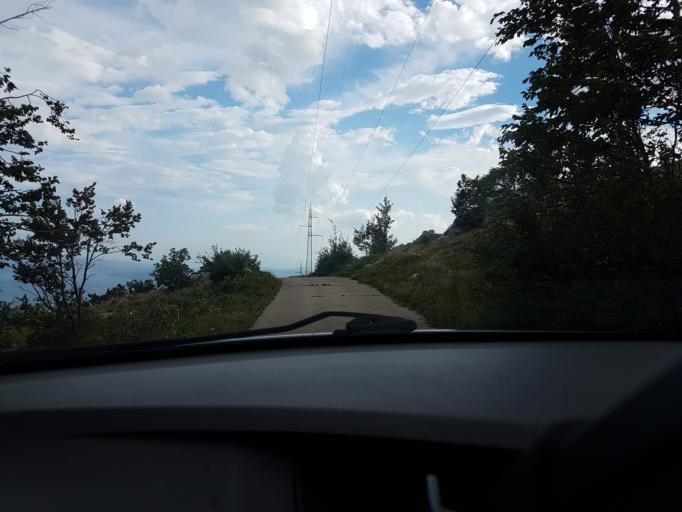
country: HR
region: Primorsko-Goranska
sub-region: Grad Crikvenica
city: Crikvenica
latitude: 45.2442
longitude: 14.6894
